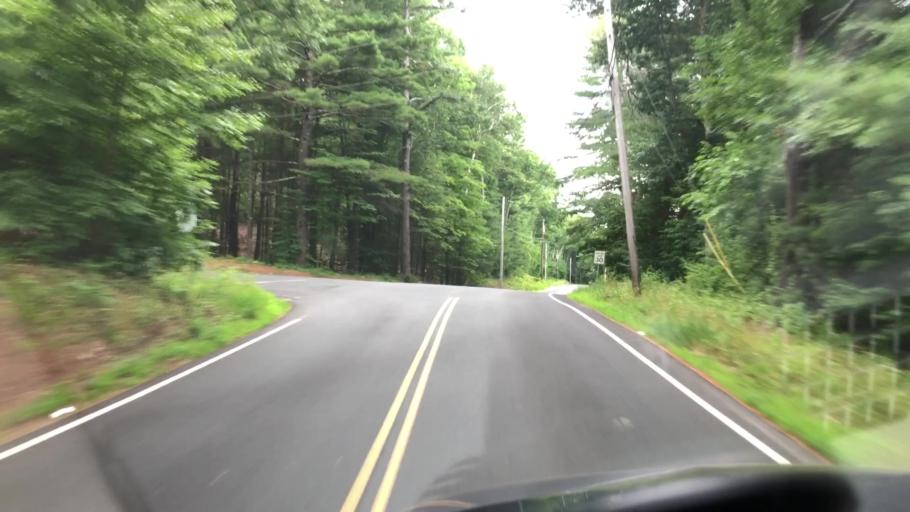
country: US
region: Massachusetts
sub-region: Hampshire County
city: Southampton
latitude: 42.1976
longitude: -72.7443
